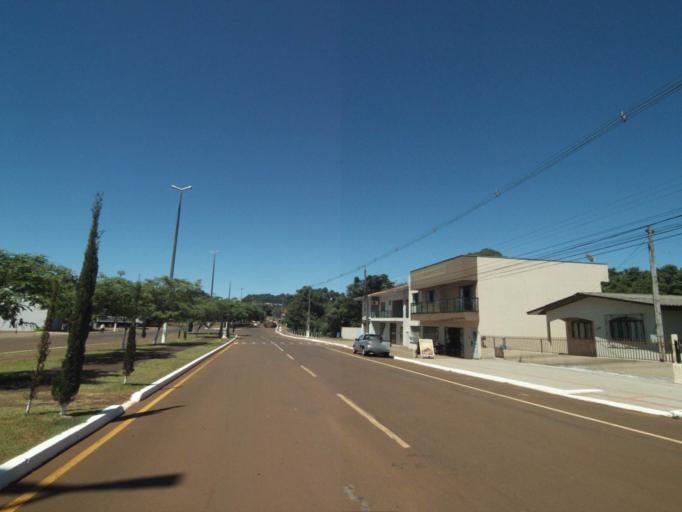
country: BR
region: Parana
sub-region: Pato Branco
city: Pato Branco
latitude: -26.2630
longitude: -52.7785
